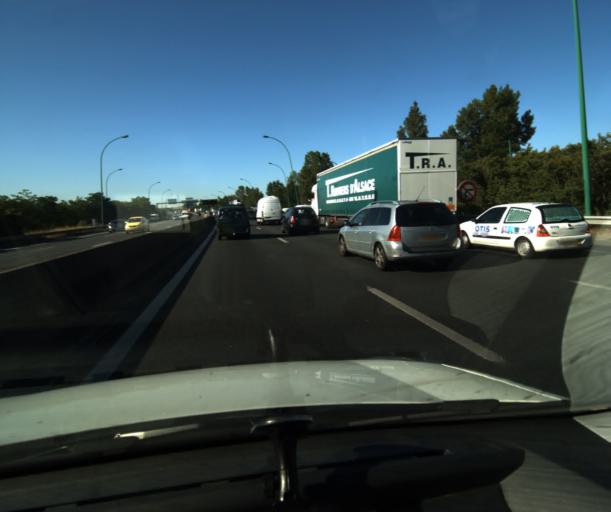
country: FR
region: Midi-Pyrenees
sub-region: Departement de la Haute-Garonne
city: Ramonville-Saint-Agne
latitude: 43.5711
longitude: 1.4943
